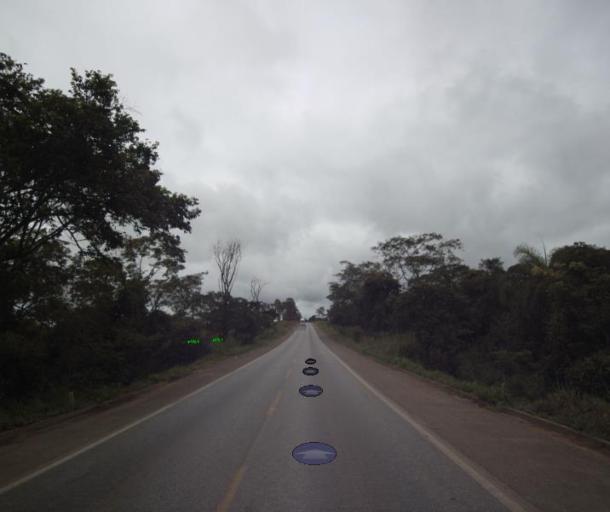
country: BR
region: Goias
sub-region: Uruacu
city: Uruacu
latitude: -14.6134
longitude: -49.1690
